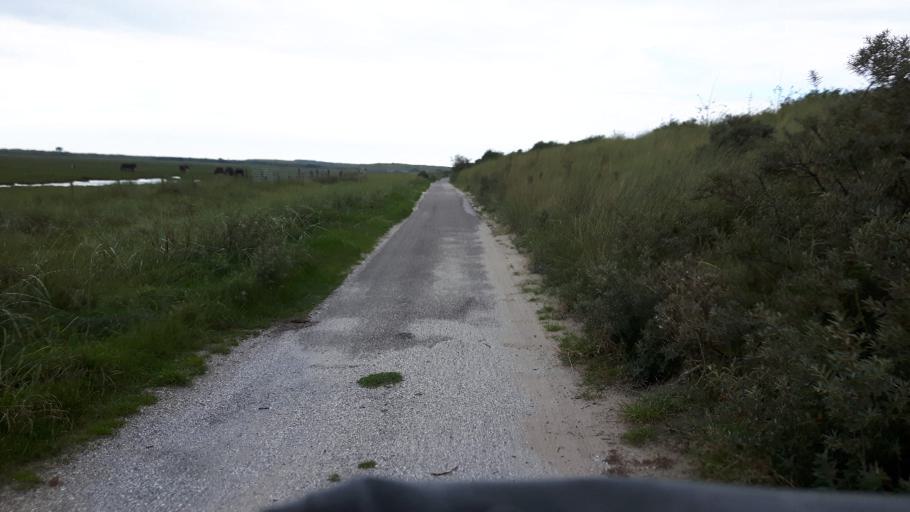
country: NL
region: Friesland
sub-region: Gemeente Ameland
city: Nes
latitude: 53.4611
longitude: 5.8490
